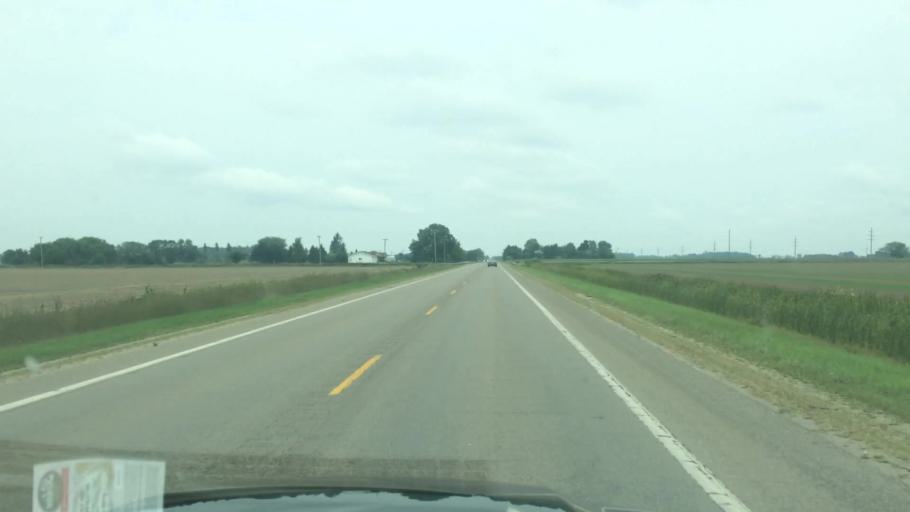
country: US
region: Michigan
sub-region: Huron County
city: Bad Axe
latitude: 43.8463
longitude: -83.0017
